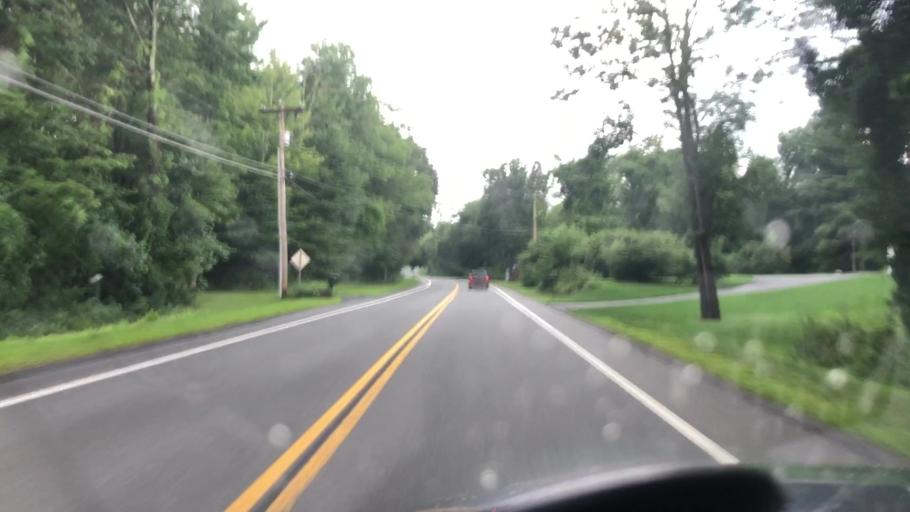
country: US
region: Massachusetts
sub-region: Hampshire County
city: Westhampton
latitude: 42.2869
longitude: -72.7533
